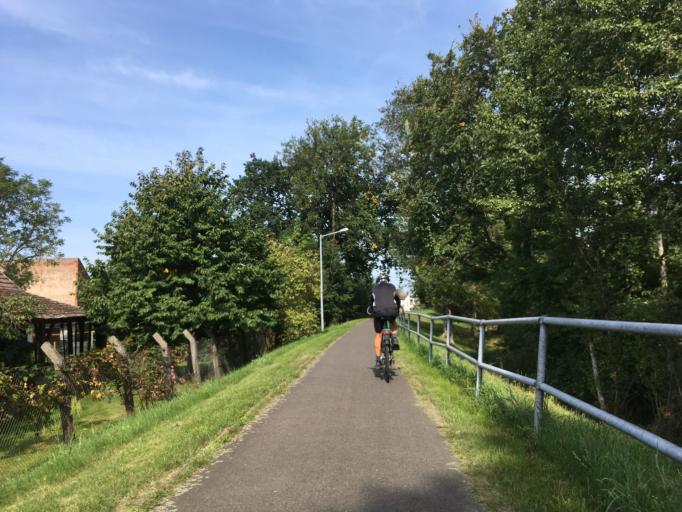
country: DE
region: Brandenburg
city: Guben
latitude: 51.9745
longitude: 14.7014
